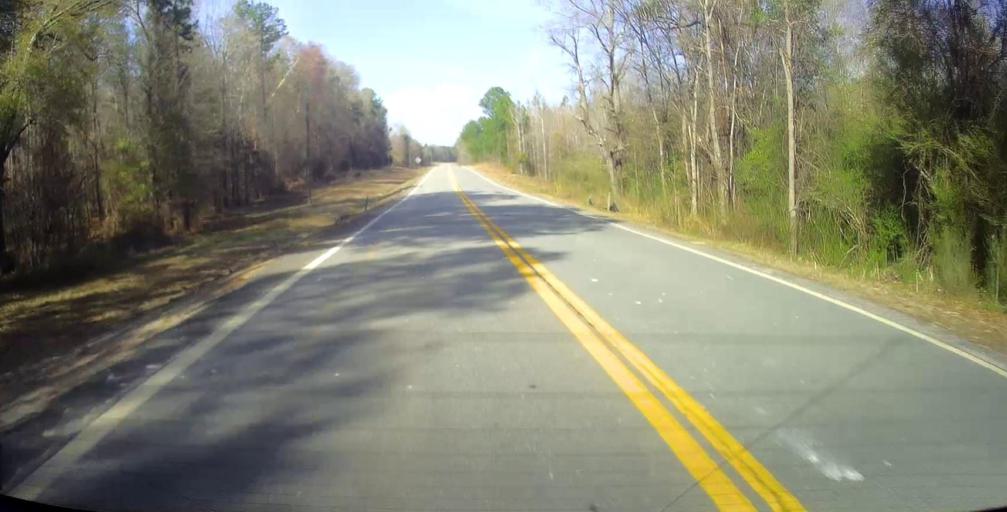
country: US
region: Georgia
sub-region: Wilkinson County
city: Gordon
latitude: 32.7911
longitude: -83.3321
